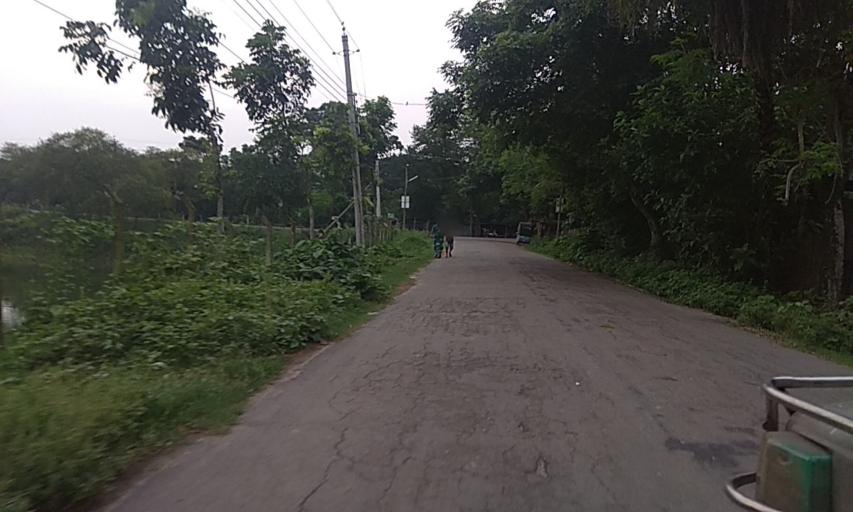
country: BD
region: Dhaka
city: Dohar
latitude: 23.4569
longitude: 90.0144
